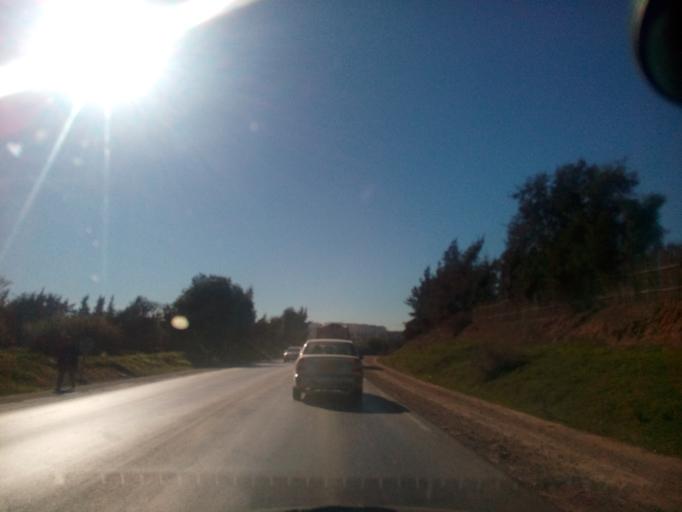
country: DZ
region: Relizane
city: Djidiouia
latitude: 35.9326
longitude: 0.8487
